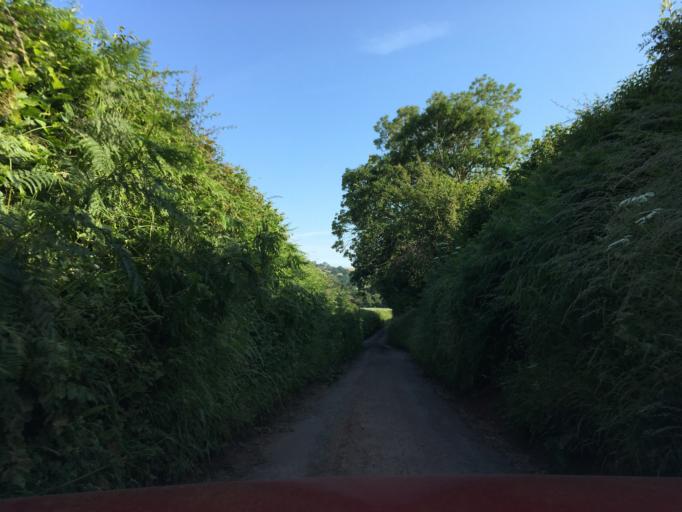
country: GB
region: England
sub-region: Gloucestershire
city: Berkeley
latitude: 51.7529
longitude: -2.4643
